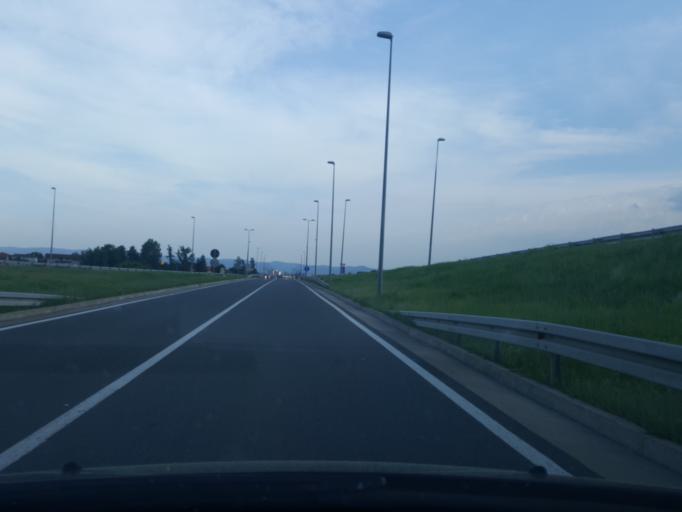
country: RS
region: Autonomna Pokrajina Vojvodina
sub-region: Juznobacki Okrug
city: Novi Sad
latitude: 45.3053
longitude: 19.8079
